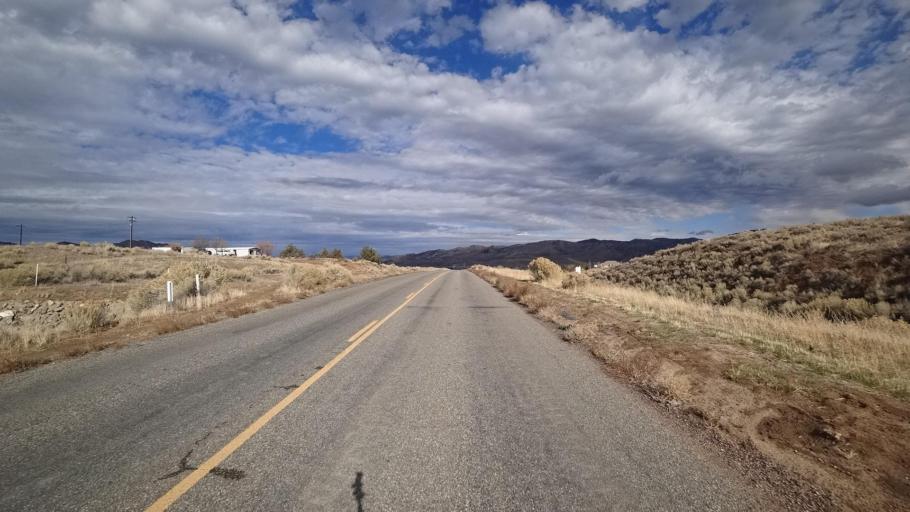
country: US
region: California
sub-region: Kern County
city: Tehachapi
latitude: 35.1145
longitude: -118.4680
